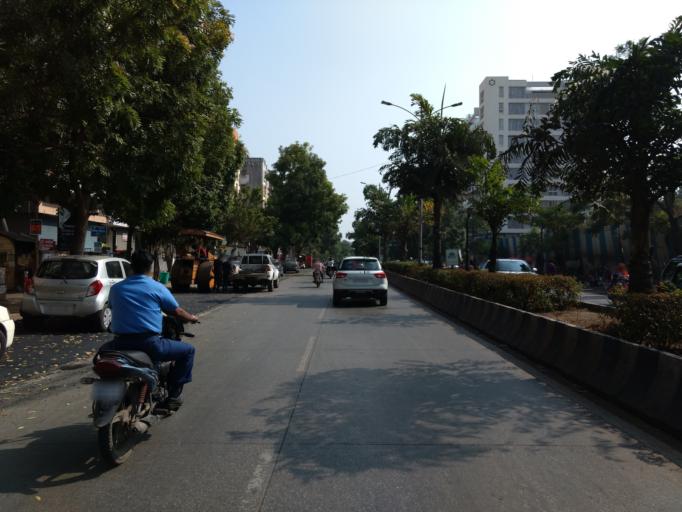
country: IN
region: Maharashtra
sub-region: Pune Division
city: Pune
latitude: 18.4809
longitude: 73.8634
